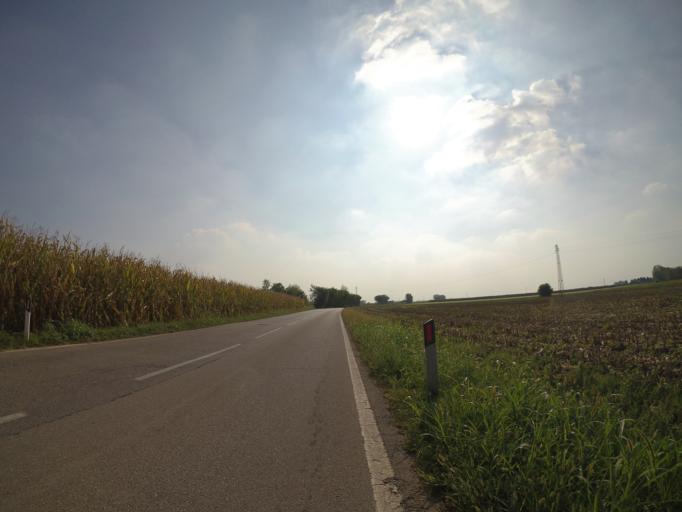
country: IT
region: Friuli Venezia Giulia
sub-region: Provincia di Udine
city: Sedegliano
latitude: 45.9918
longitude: 13.0180
